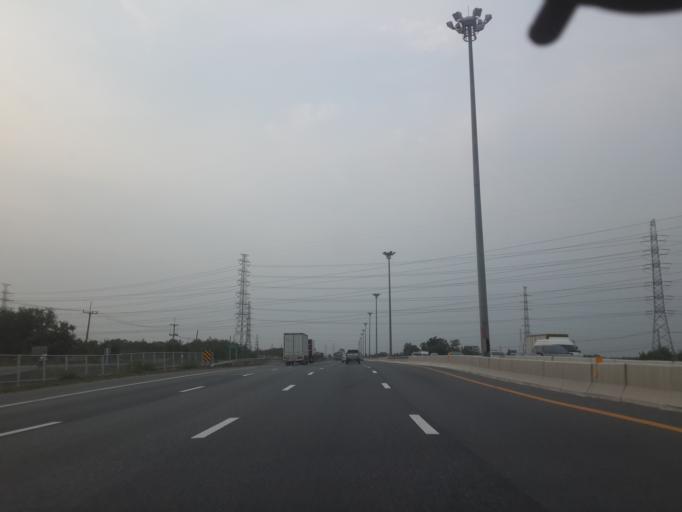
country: TH
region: Chachoengsao
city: Bang Pakong
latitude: 13.5076
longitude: 101.0354
